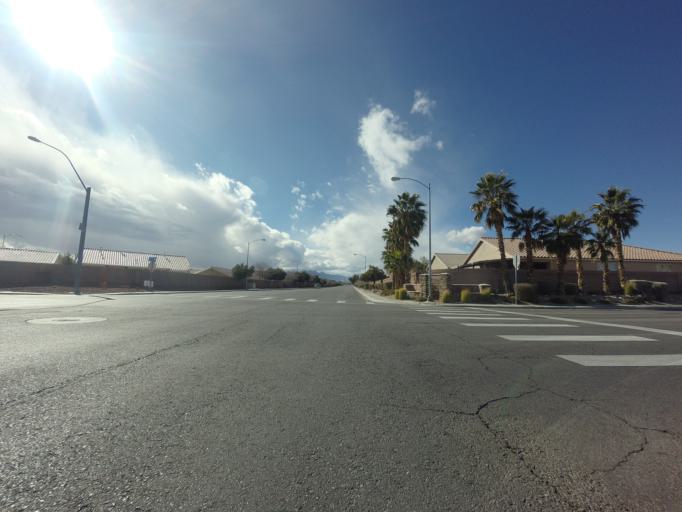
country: US
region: Nevada
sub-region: Clark County
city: North Las Vegas
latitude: 36.2543
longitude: -115.1258
